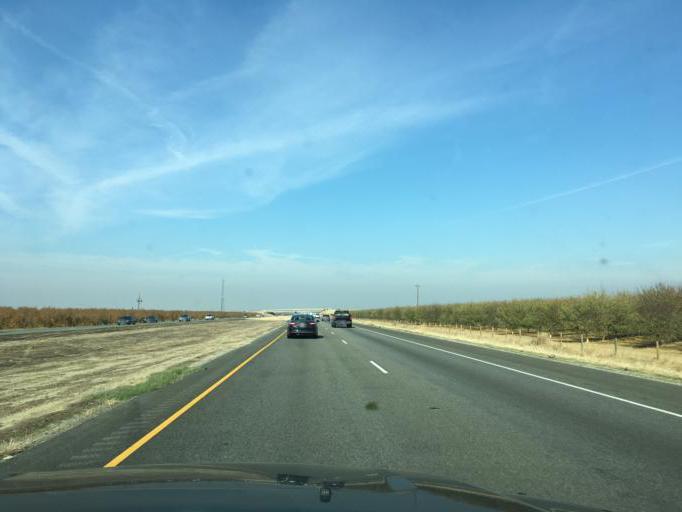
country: US
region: California
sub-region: Kern County
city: Weedpatch
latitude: 35.0714
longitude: -119.0119
